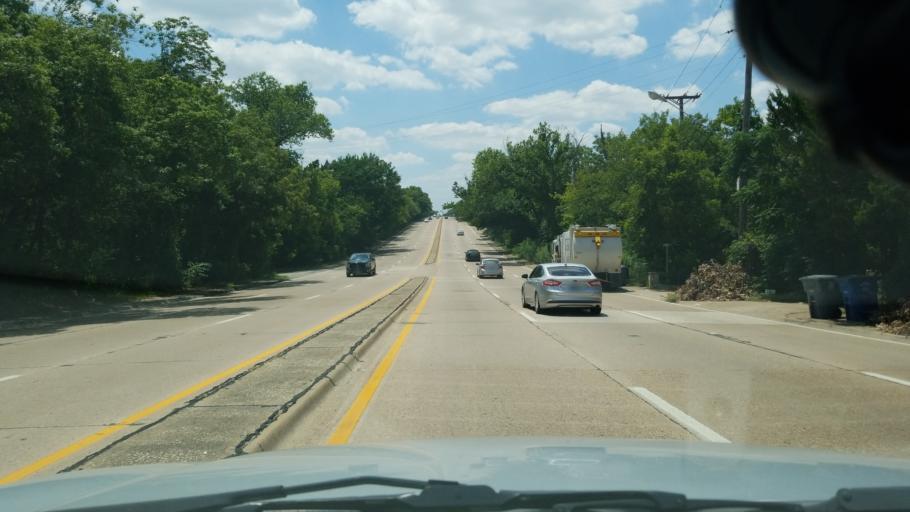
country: US
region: Texas
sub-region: Dallas County
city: Cockrell Hill
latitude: 32.6913
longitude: -96.8662
